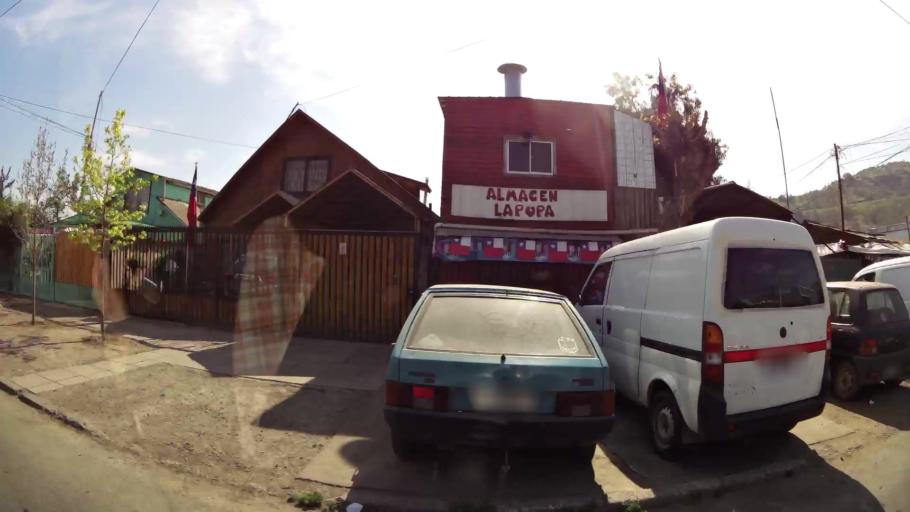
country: CL
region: Santiago Metropolitan
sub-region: Provincia de Santiago
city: Santiago
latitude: -33.3986
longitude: -70.6229
